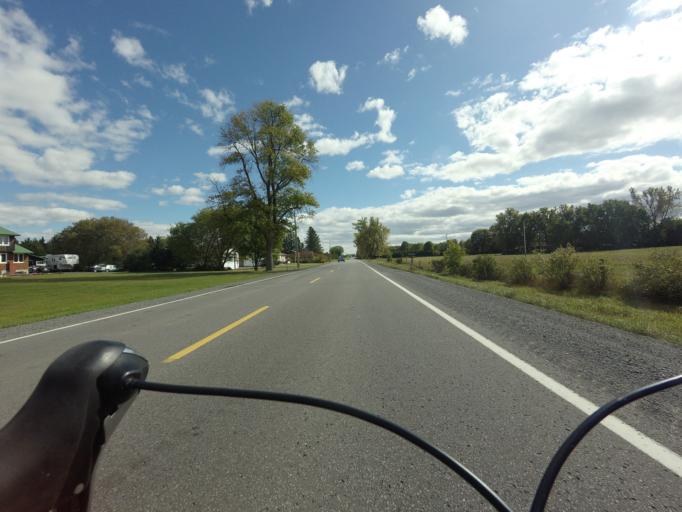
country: CA
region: Ontario
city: Bells Corners
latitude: 45.1868
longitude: -75.6765
